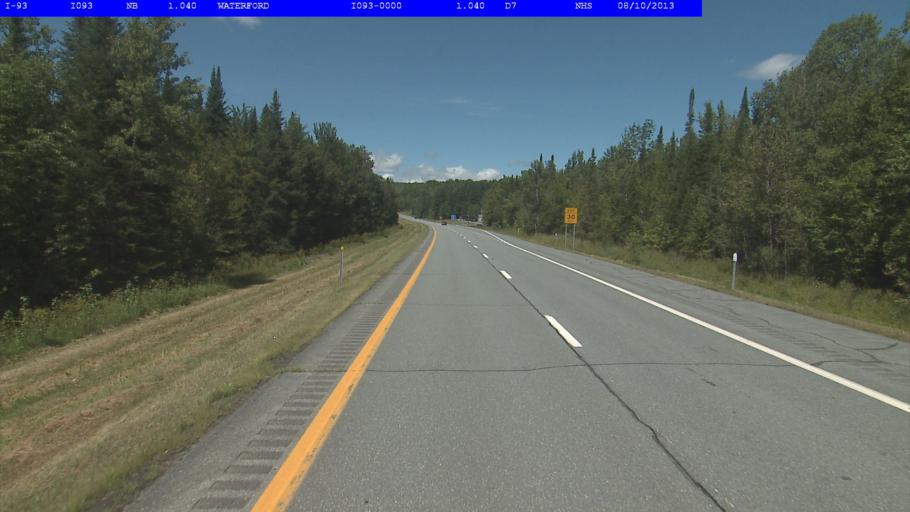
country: US
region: Vermont
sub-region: Caledonia County
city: Saint Johnsbury
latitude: 44.3576
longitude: -71.8966
